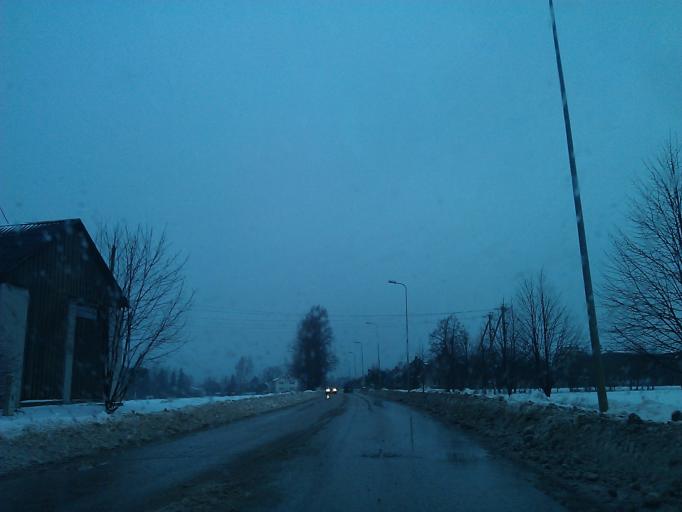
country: LV
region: Cesu Rajons
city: Cesis
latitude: 57.3012
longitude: 25.2959
